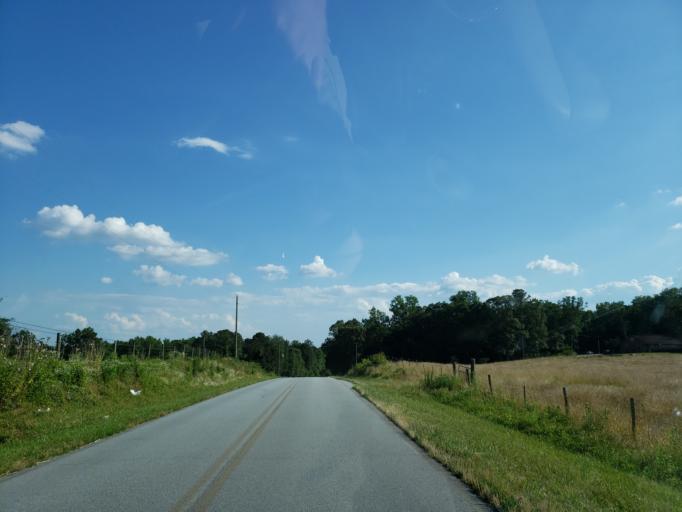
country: US
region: Georgia
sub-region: Carroll County
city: Carrollton
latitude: 33.6559
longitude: -85.0881
